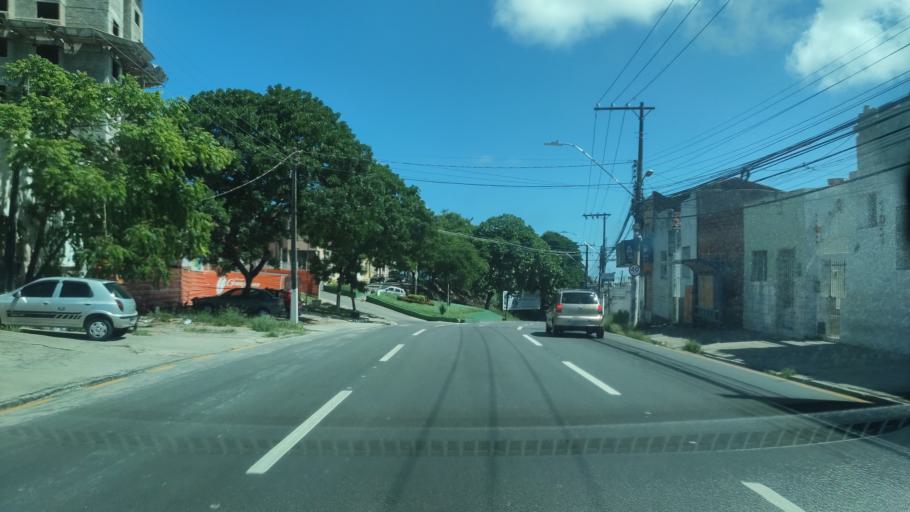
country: BR
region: Alagoas
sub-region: Maceio
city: Maceio
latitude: -9.6586
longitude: -35.7362
